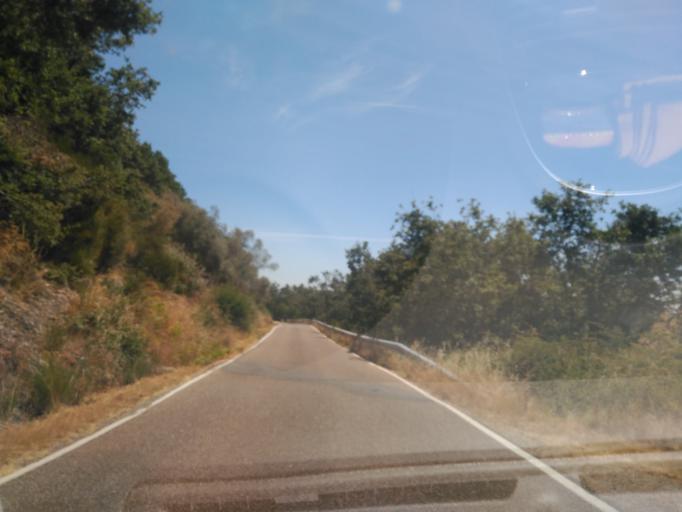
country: ES
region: Castille and Leon
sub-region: Provincia de Zamora
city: Galende
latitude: 42.1340
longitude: -6.7132
